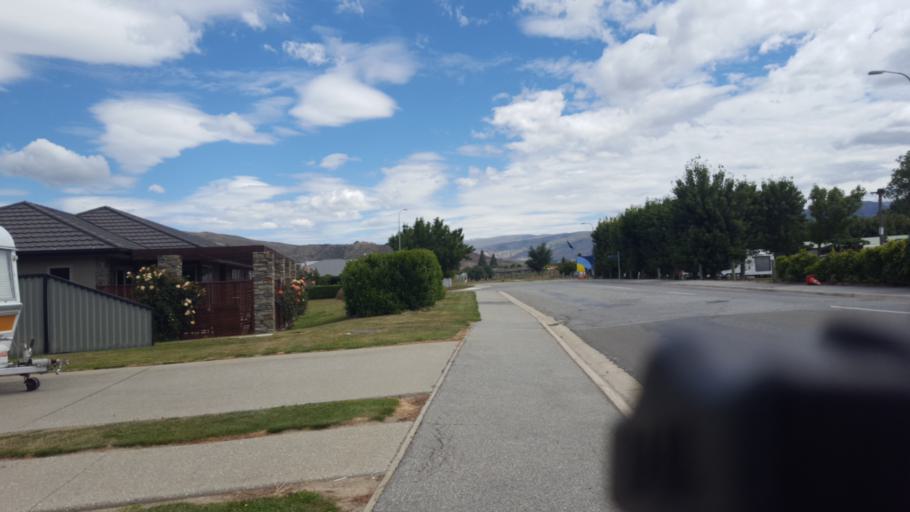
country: NZ
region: Otago
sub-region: Queenstown-Lakes District
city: Wanaka
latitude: -45.0395
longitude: 169.2155
